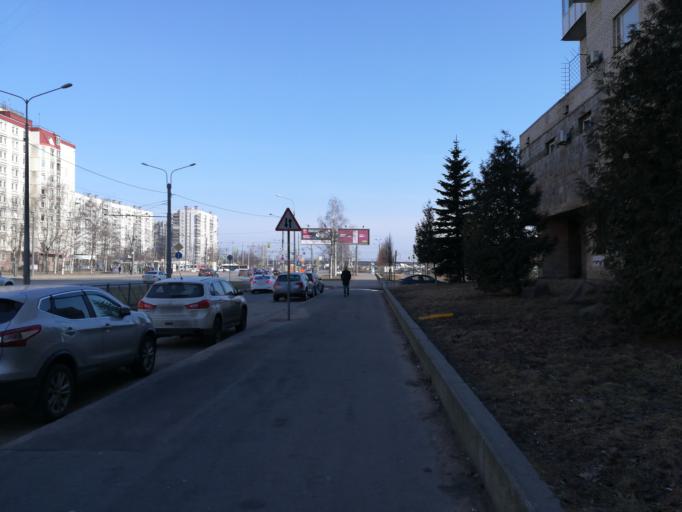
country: RU
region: St.-Petersburg
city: Vasyl'evsky Ostrov
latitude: 59.9536
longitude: 30.2355
